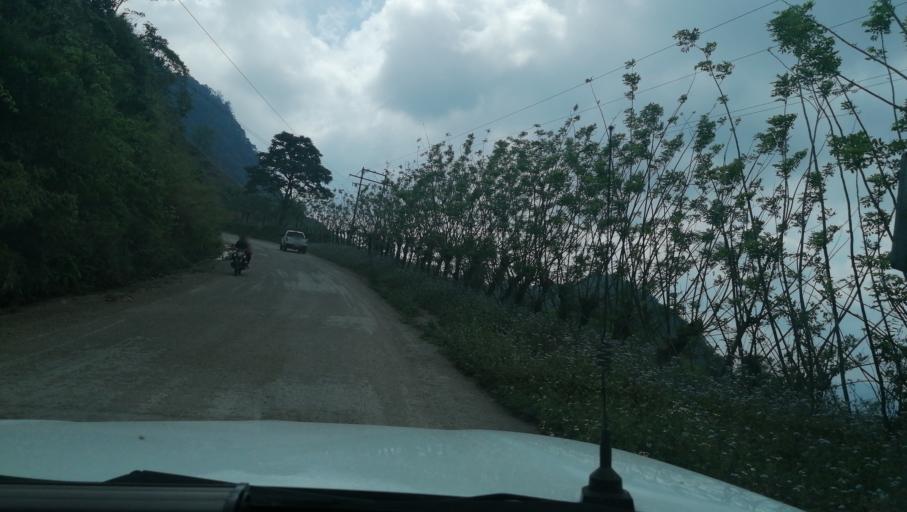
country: MX
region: Chiapas
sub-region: Francisco Leon
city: San Miguel la Sardina
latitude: 17.2491
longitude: -93.2837
